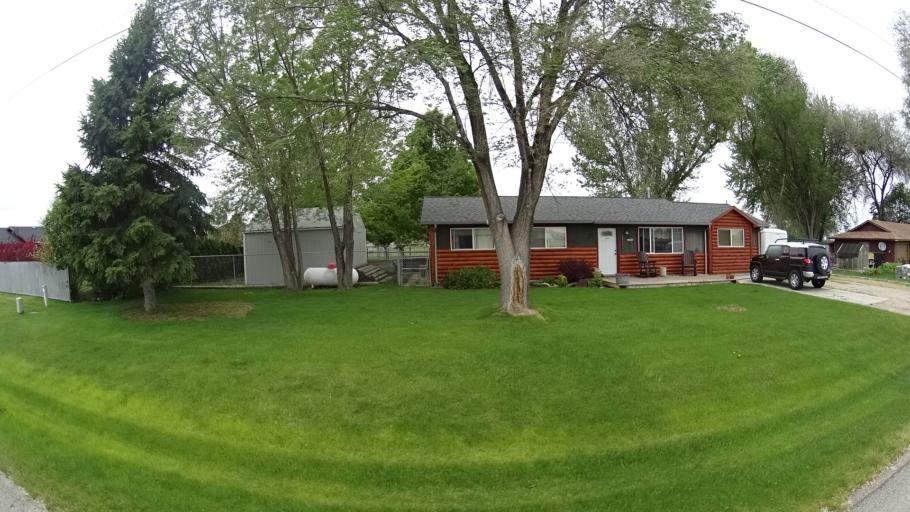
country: US
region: Idaho
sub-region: Ada County
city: Kuna
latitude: 43.4854
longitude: -116.3144
